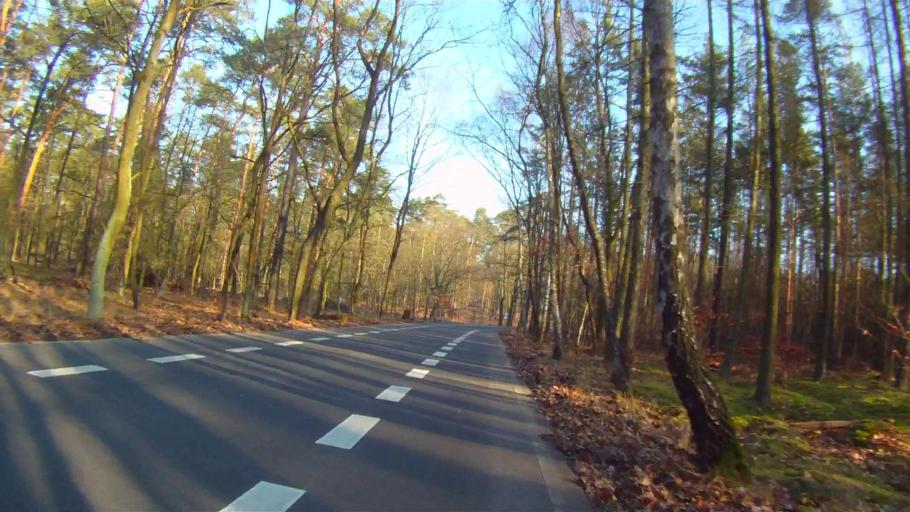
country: DE
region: Berlin
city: Muggelheim
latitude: 52.4287
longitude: 13.6663
